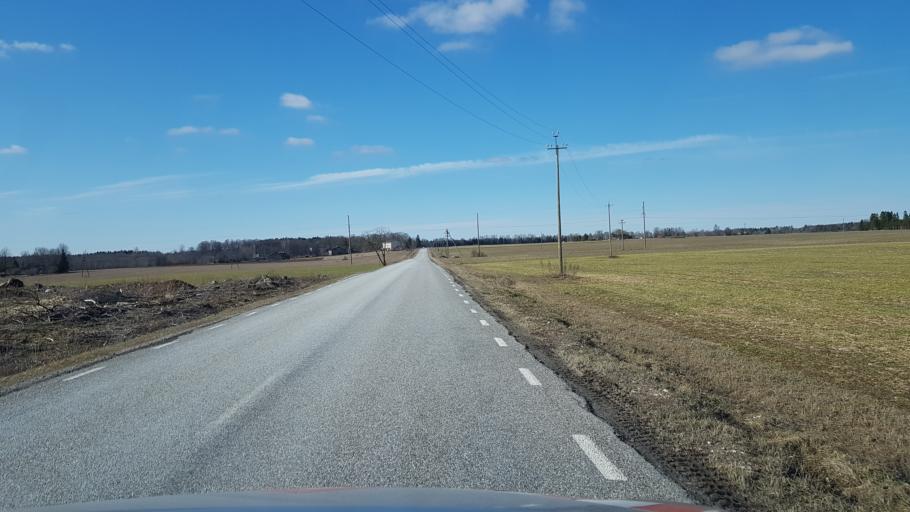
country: EE
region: Laeaene-Virumaa
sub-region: Tapa vald
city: Tapa
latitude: 59.2658
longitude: 26.0139
